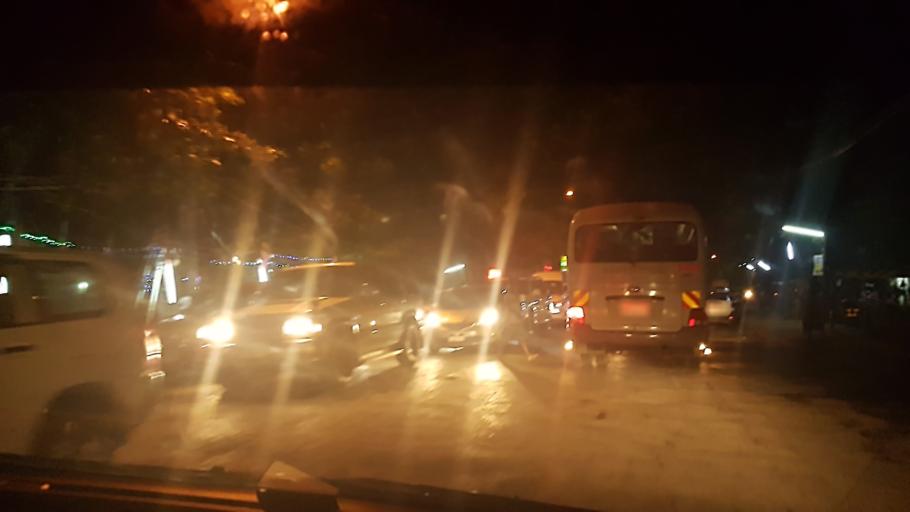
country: MM
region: Yangon
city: Yangon
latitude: 16.8172
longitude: 96.1267
